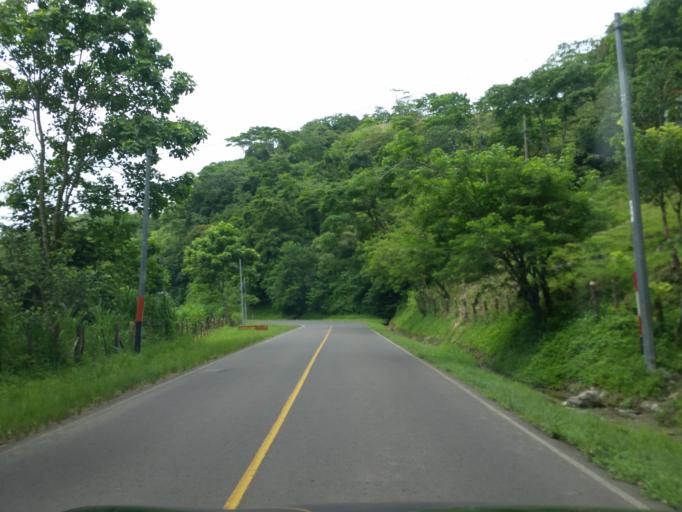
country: NI
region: Matagalpa
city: San Ramon
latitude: 13.0301
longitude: -85.7794
